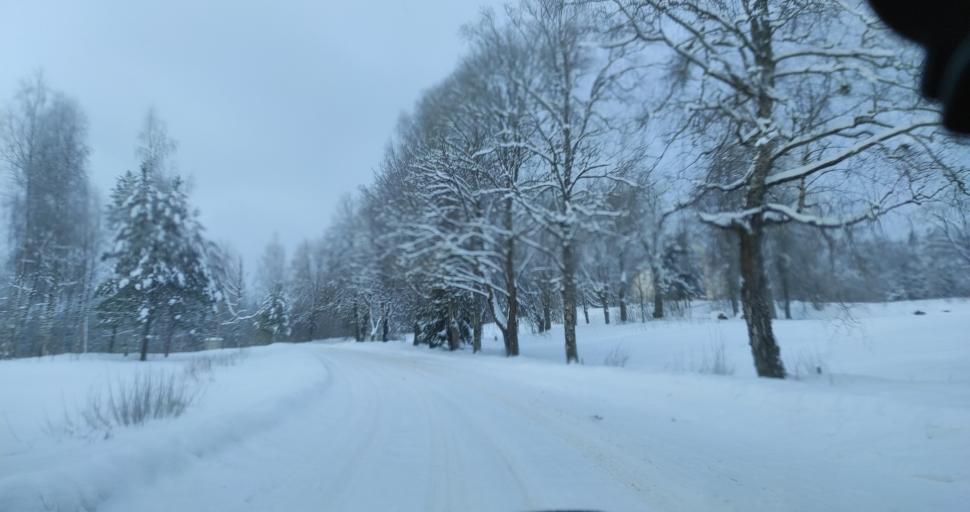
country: LV
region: Madonas Rajons
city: Madona
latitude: 56.8704
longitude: 25.9839
